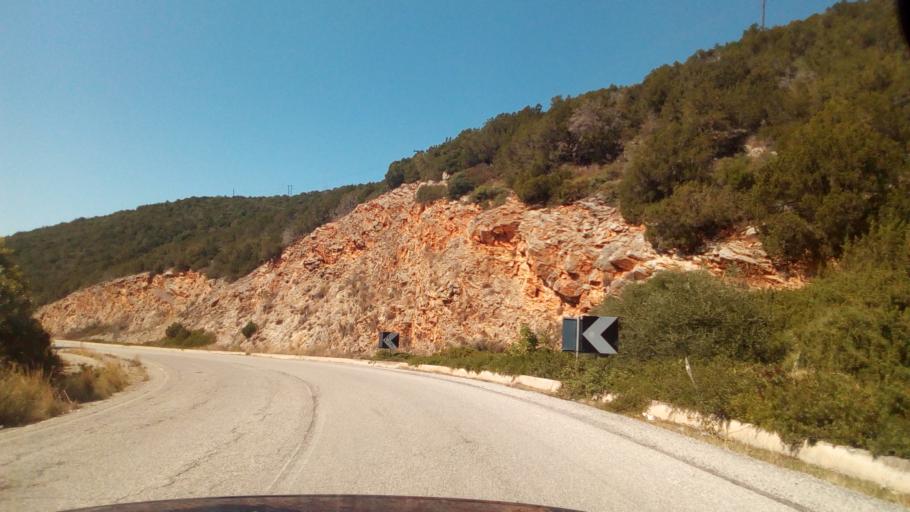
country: GR
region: West Greece
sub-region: Nomos Achaias
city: Selianitika
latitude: 38.3717
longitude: 22.1039
